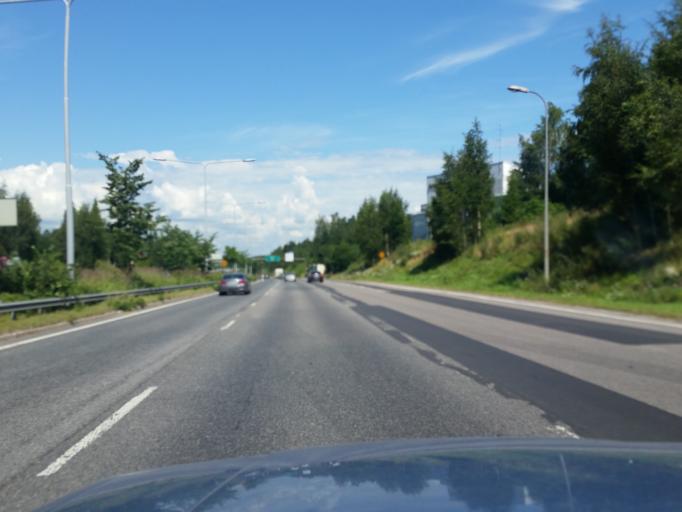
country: FI
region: Uusimaa
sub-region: Helsinki
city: Helsinki
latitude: 60.2225
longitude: 24.9455
